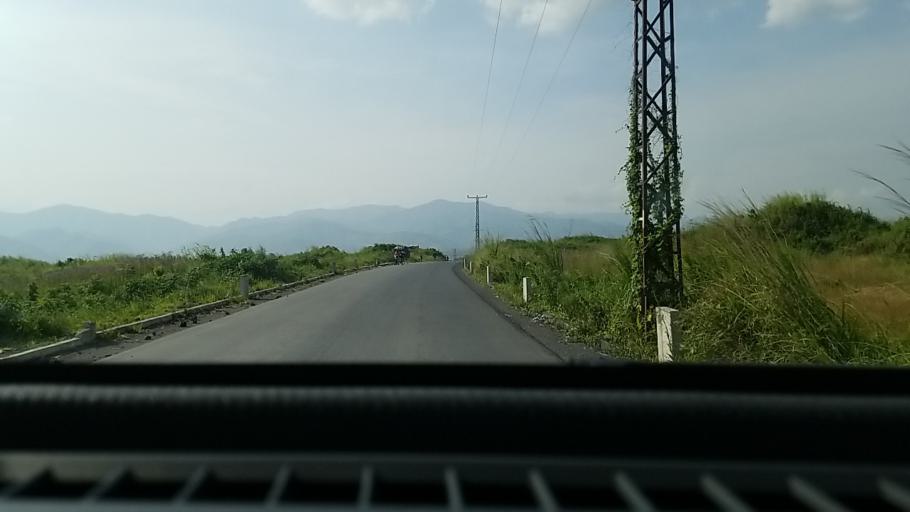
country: CD
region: Nord Kivu
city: Sake
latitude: -1.5929
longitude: 29.0990
